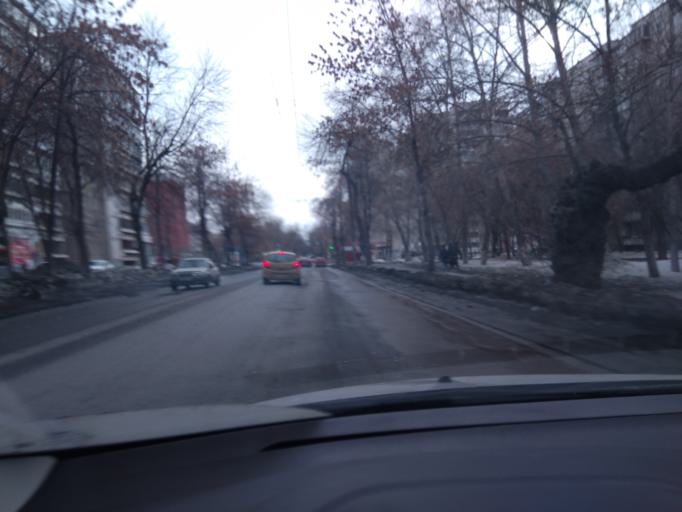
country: RU
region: Sverdlovsk
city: Yekaterinburg
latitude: 56.8930
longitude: 60.6021
